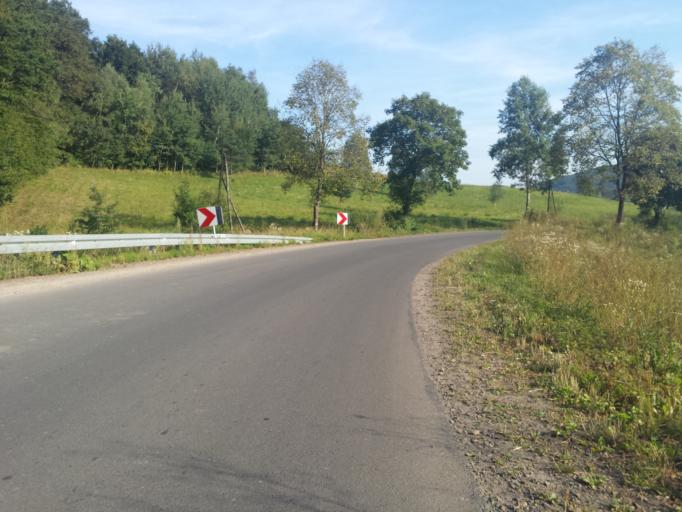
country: PL
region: Subcarpathian Voivodeship
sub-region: Powiat leski
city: Uherce Mineralne
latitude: 49.4501
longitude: 22.3920
